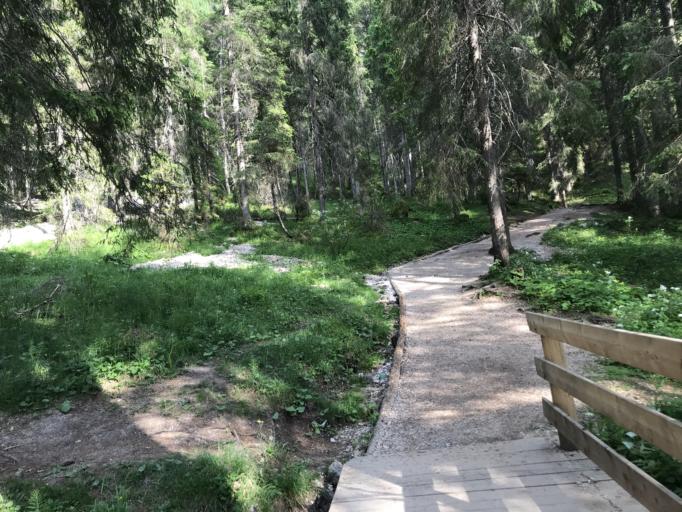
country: IT
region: Trentino-Alto Adige
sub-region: Bolzano
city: Braies
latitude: 46.6978
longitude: 12.0883
